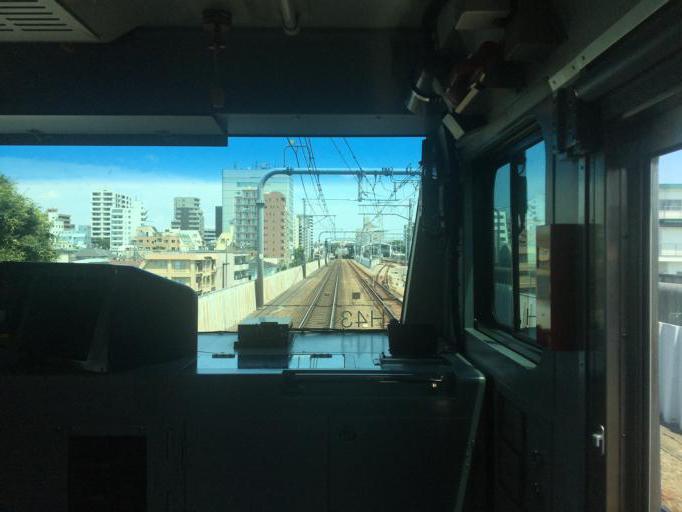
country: JP
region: Tokyo
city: Kamirenjaku
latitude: 35.7021
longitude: 139.5396
